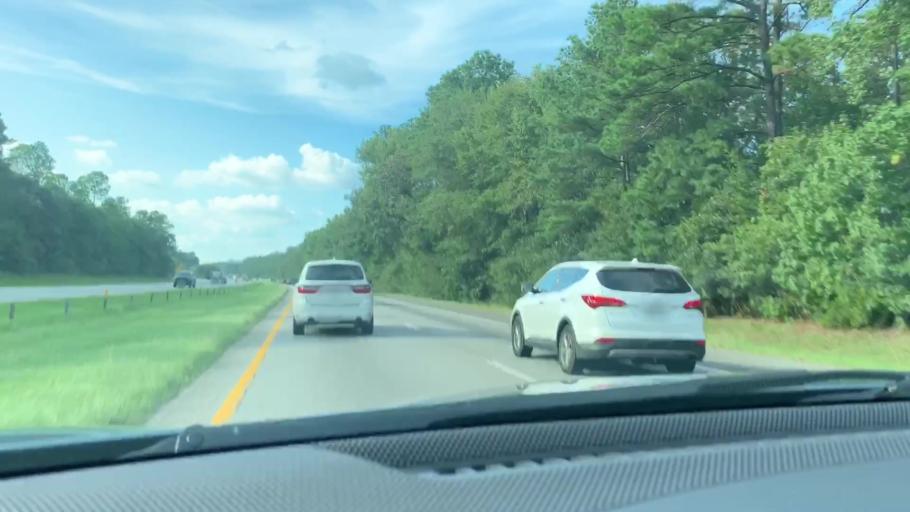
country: US
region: South Carolina
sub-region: Orangeburg County
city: Brookdale
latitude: 33.4972
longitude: -80.7673
